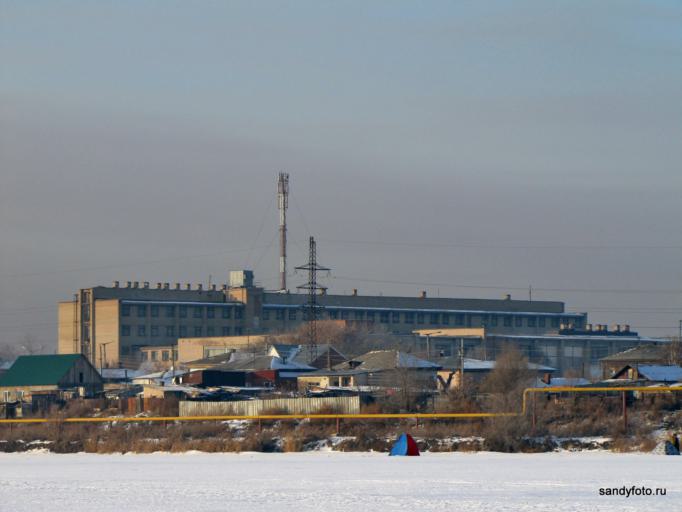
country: RU
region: Chelyabinsk
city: Troitsk
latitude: 54.0796
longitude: 61.5737
